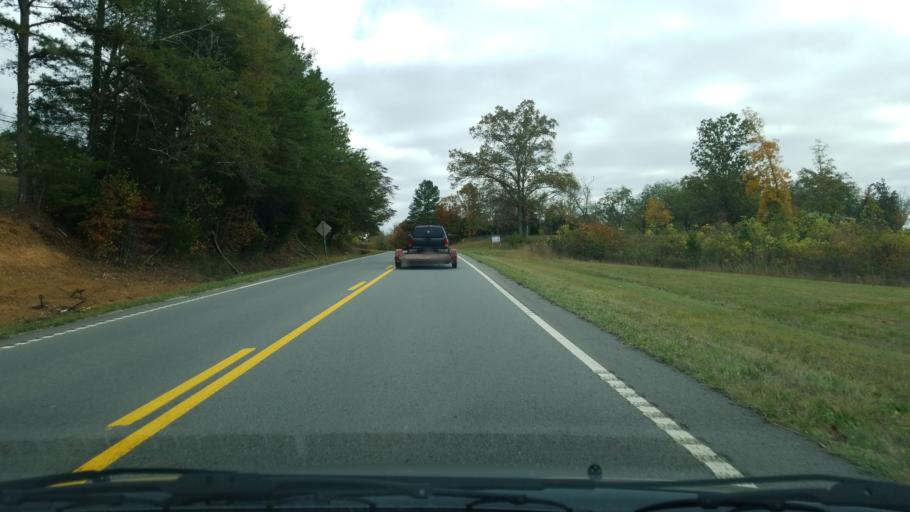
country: US
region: Tennessee
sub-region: Bradley County
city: Hopewell
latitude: 35.3247
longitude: -84.9686
